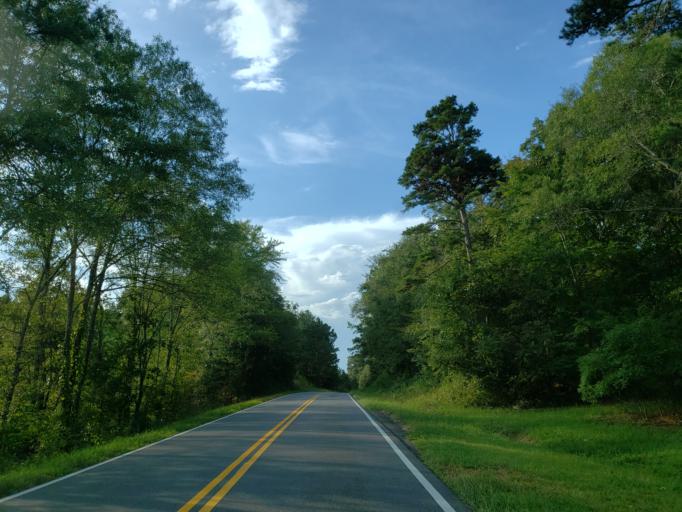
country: US
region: Georgia
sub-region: Bartow County
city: Euharlee
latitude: 34.1944
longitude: -84.9849
